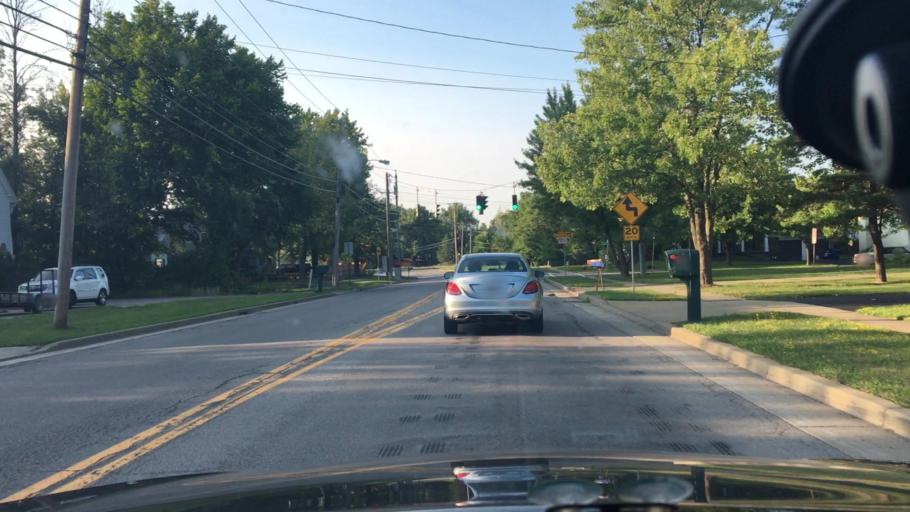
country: US
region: New York
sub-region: Erie County
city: Williamsville
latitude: 43.0015
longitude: -78.7608
